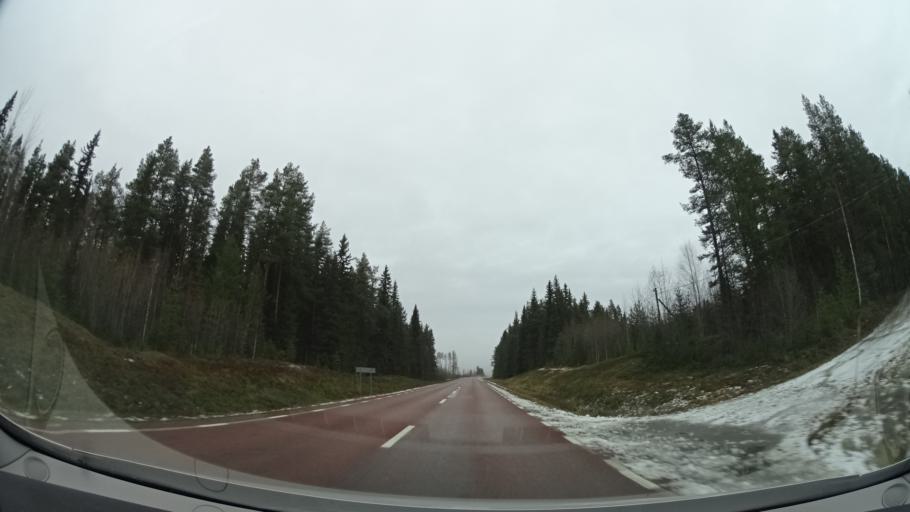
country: SE
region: Vaesterbotten
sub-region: Dorotea Kommun
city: Dorotea
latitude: 64.1715
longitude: 16.2870
